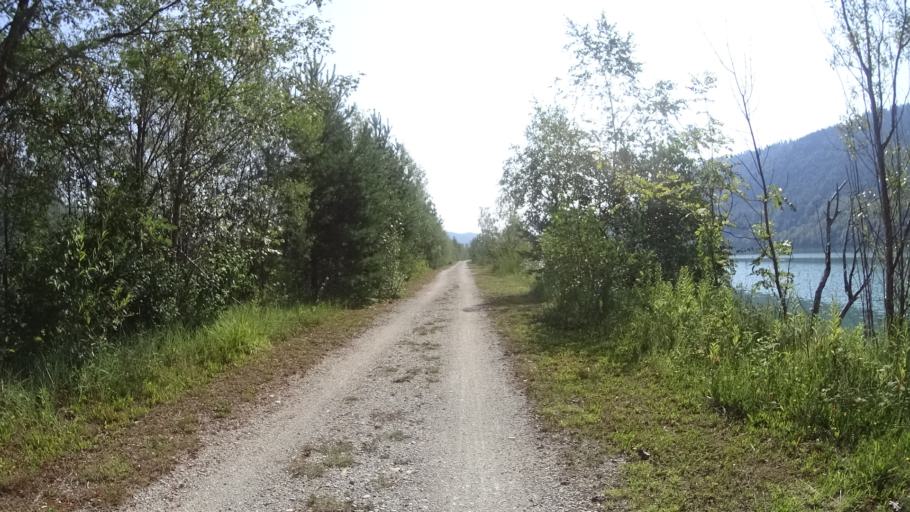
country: AT
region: Carinthia
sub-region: Politischer Bezirk Klagenfurt Land
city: Grafenstein
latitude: 46.5631
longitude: 14.4675
